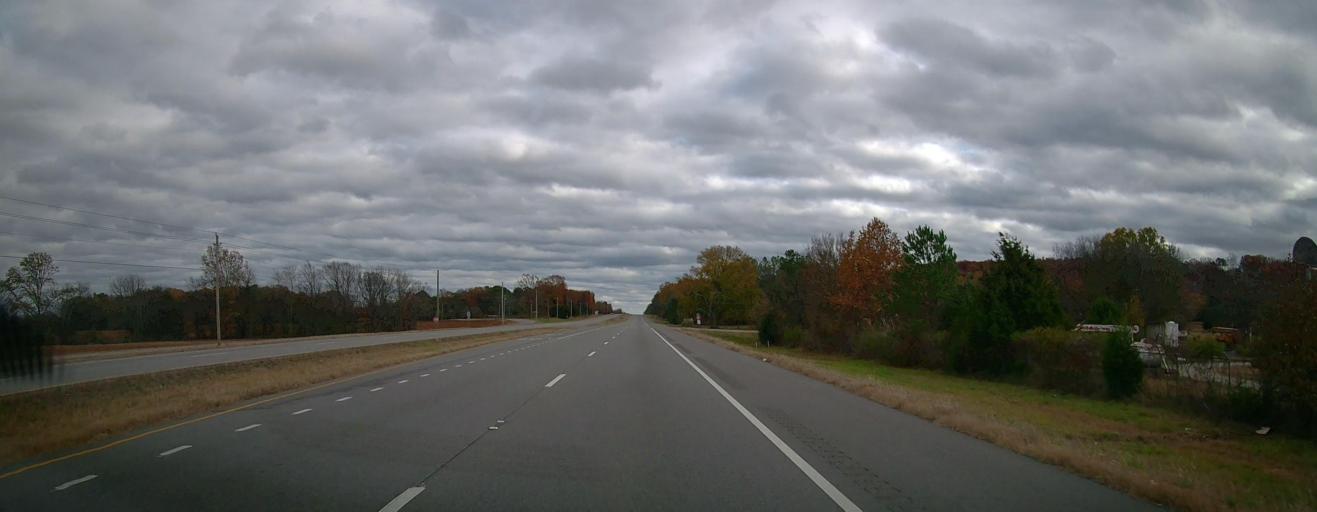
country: US
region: Alabama
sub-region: Colbert County
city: Muscle Shoals
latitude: 34.6714
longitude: -87.5639
